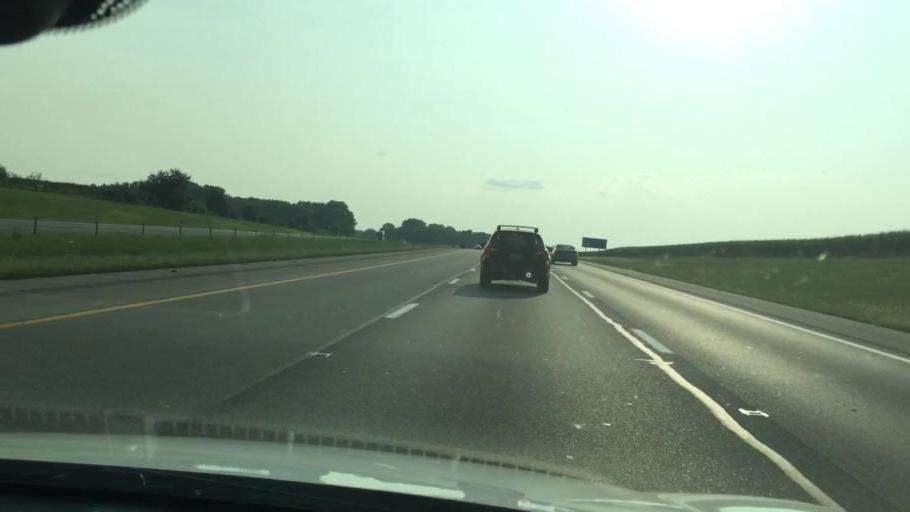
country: US
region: Ohio
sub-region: Clark County
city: Lisbon
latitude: 39.9357
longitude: -83.6658
